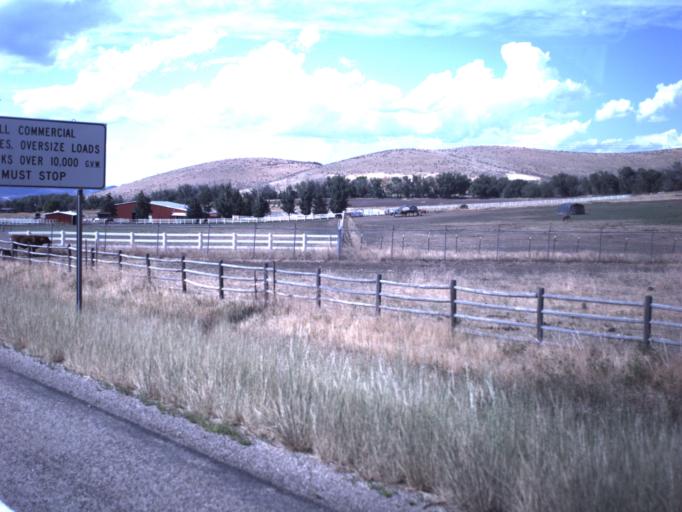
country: US
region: Utah
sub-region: Wasatch County
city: Heber
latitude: 40.4557
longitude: -111.3753
